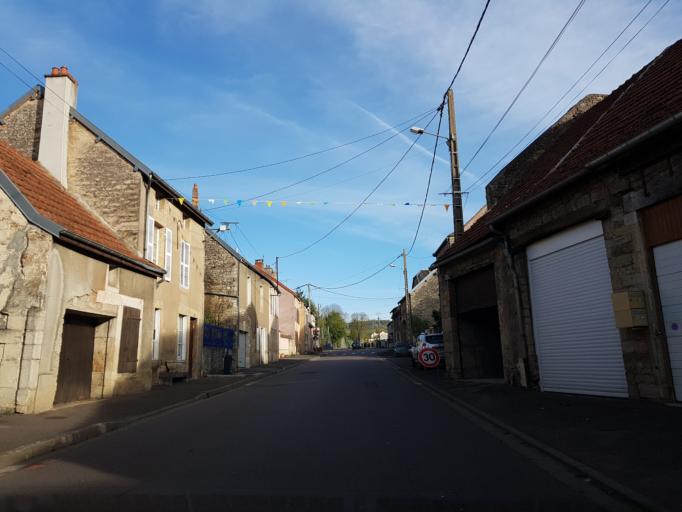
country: FR
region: Bourgogne
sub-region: Departement de la Cote-d'Or
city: Vitteaux
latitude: 47.3960
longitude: 4.5446
